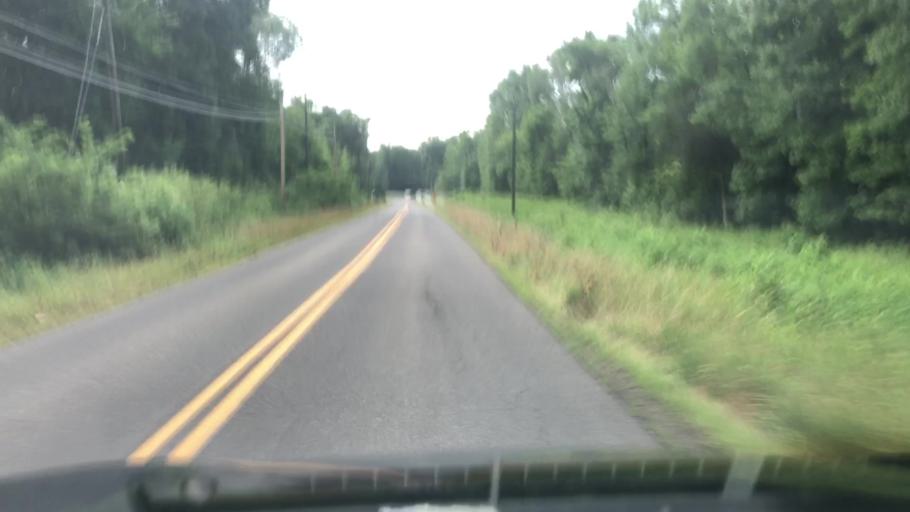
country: US
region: Virginia
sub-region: Fauquier County
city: New Baltimore
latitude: 38.7557
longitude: -77.6895
